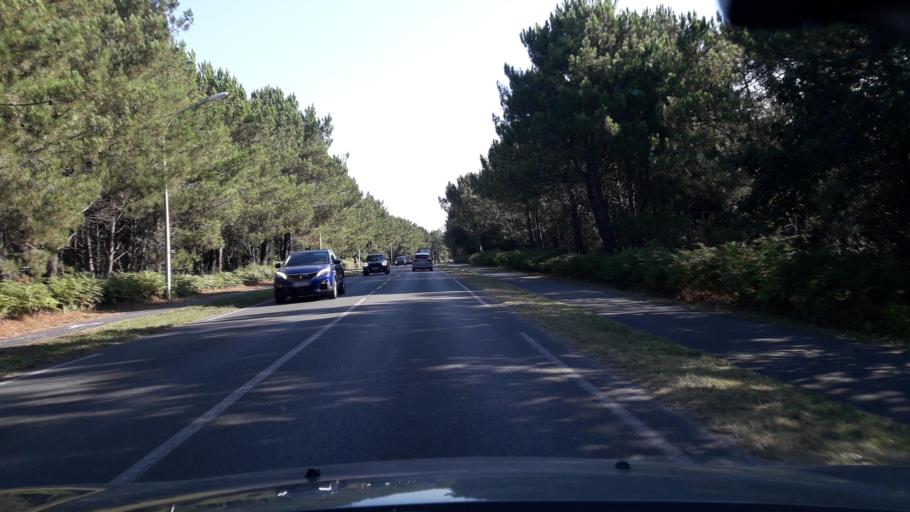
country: FR
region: Poitou-Charentes
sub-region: Departement de la Charente-Maritime
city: Les Mathes
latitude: 45.7055
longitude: -1.1648
